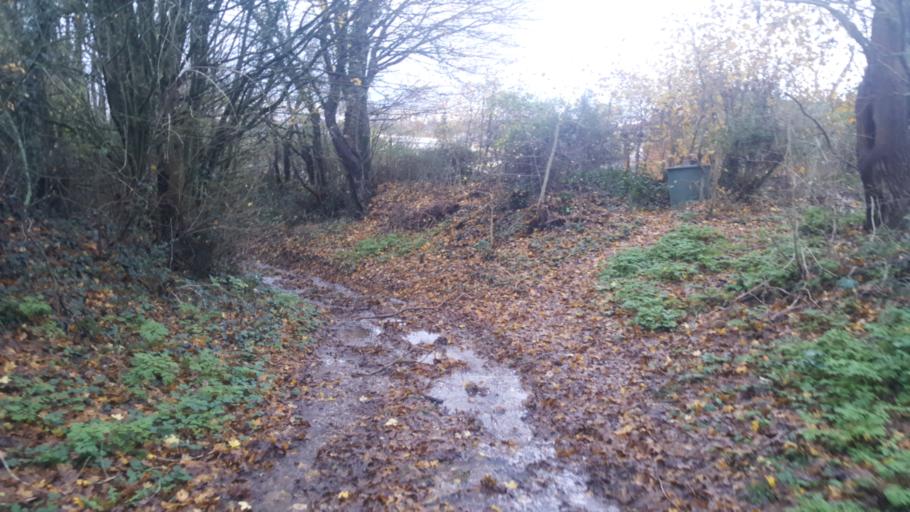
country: FR
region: Poitou-Charentes
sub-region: Departement des Deux-Sevres
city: Melle
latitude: 46.2325
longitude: -0.1271
